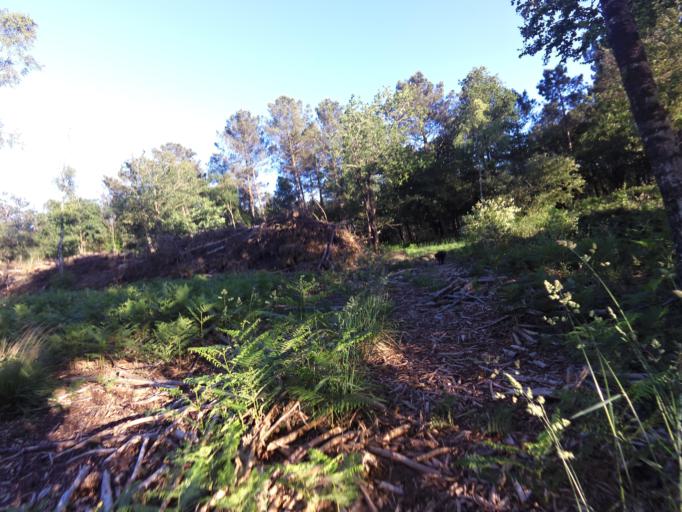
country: FR
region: Brittany
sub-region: Departement du Morbihan
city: Molac
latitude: 47.7405
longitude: -2.4311
